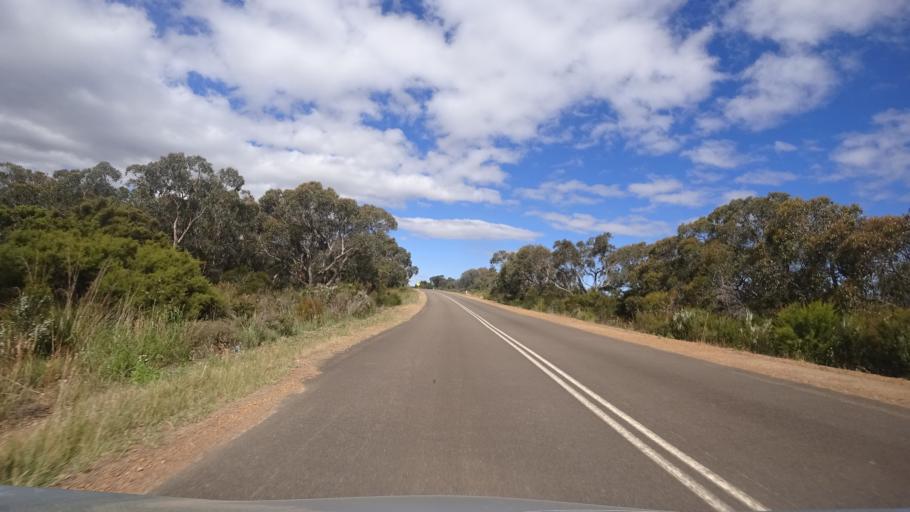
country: AU
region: South Australia
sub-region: Kangaroo Island
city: Kingscote
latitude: -35.8031
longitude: 137.0571
